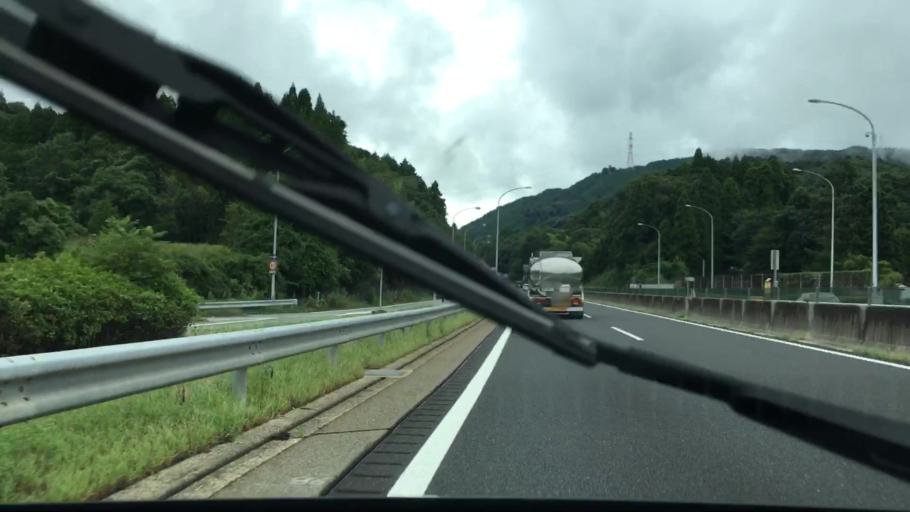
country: JP
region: Hyogo
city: Yamazakicho-nakabirose
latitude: 35.0318
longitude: 134.4854
